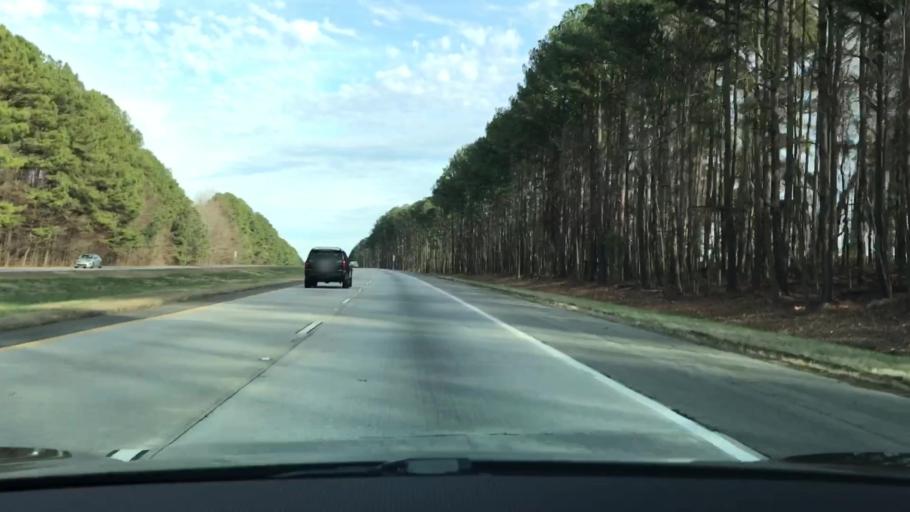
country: US
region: Georgia
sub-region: Taliaferro County
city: Crawfordville
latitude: 33.5277
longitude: -82.9507
